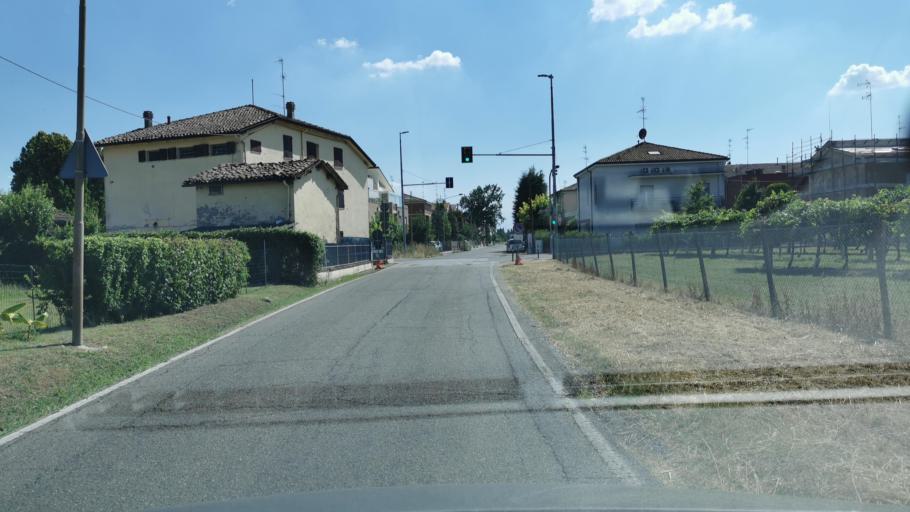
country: IT
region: Emilia-Romagna
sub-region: Provincia di Modena
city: Fossoli
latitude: 44.8197
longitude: 10.8978
